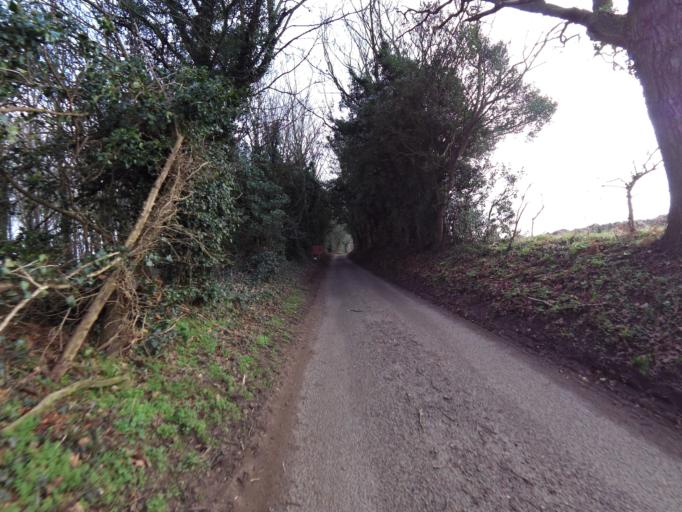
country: GB
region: England
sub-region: Suffolk
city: Woodbridge
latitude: 52.0680
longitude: 1.3029
